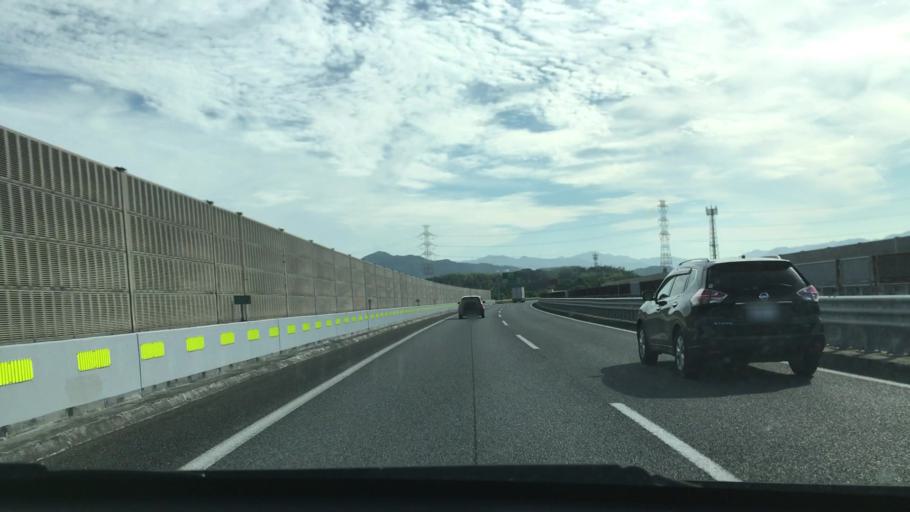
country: JP
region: Fukuoka
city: Kanda
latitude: 33.8354
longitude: 130.9212
